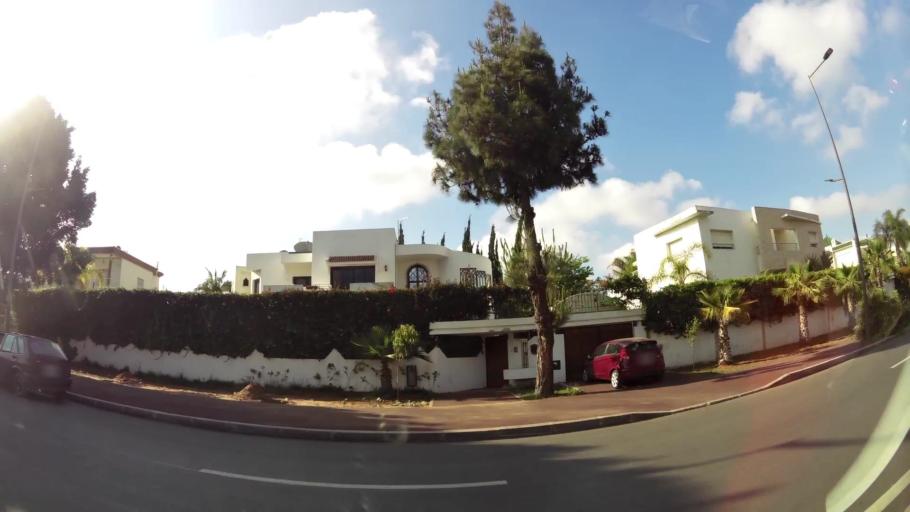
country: MA
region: Rabat-Sale-Zemmour-Zaer
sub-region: Skhirate-Temara
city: Temara
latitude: 33.9496
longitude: -6.8658
